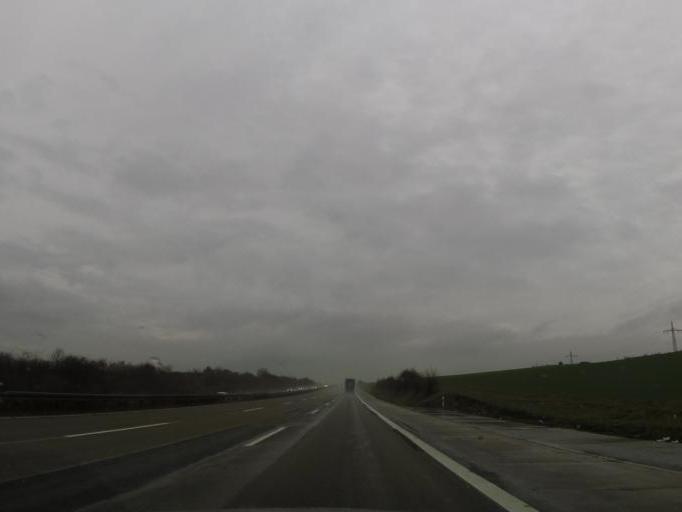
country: DE
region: Hesse
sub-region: Regierungsbezirk Giessen
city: Villmar
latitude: 50.3373
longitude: 8.1875
